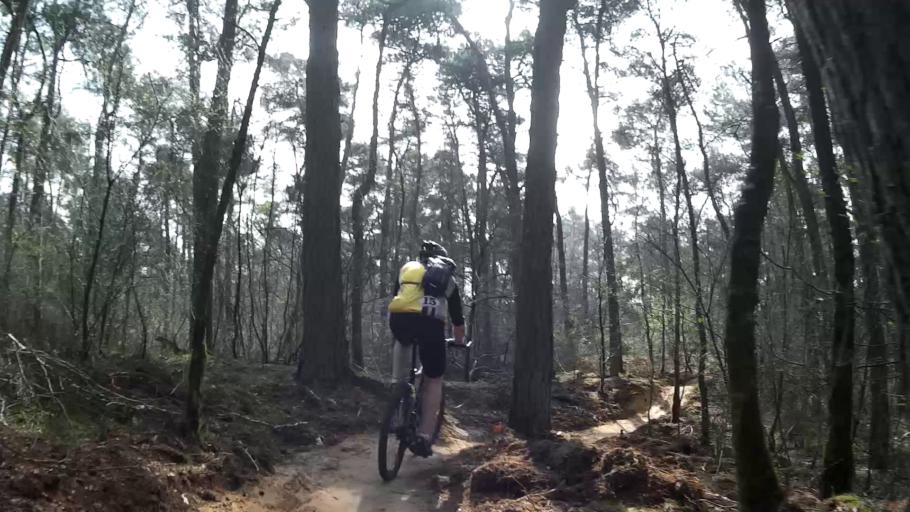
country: NL
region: Utrecht
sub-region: Gemeente Utrechtse Heuvelrug
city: Driebergen-Rijsenburg
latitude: 52.0718
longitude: 5.3122
